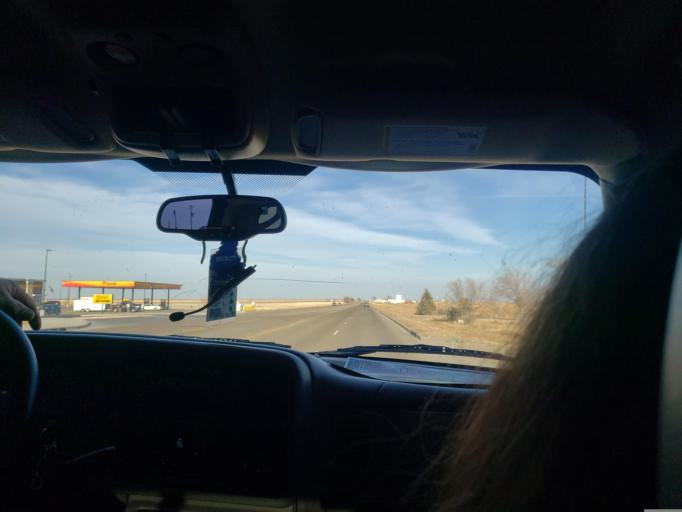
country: US
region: Oklahoma
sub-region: Texas County
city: Goodwell
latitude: 36.5050
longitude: -101.7747
